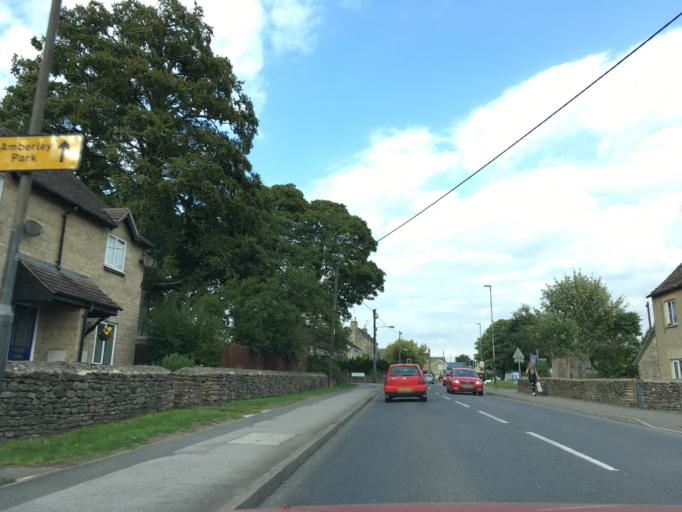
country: GB
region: England
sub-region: Gloucestershire
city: Tetbury
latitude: 51.6421
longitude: -2.1586
